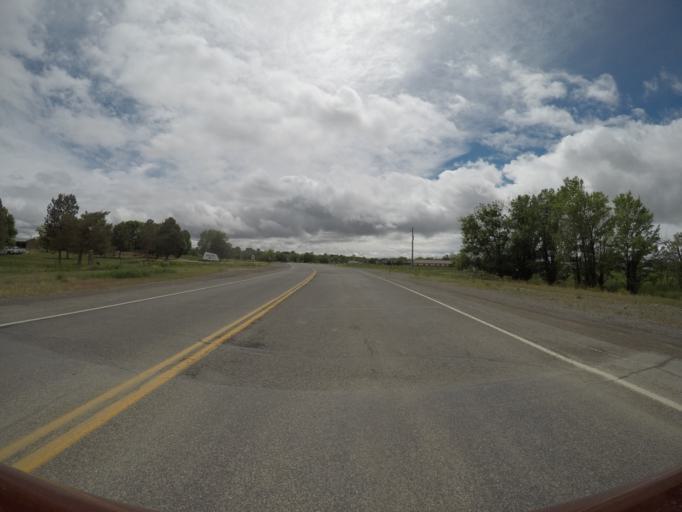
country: US
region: Wyoming
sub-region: Big Horn County
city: Lovell
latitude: 44.8390
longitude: -108.3777
